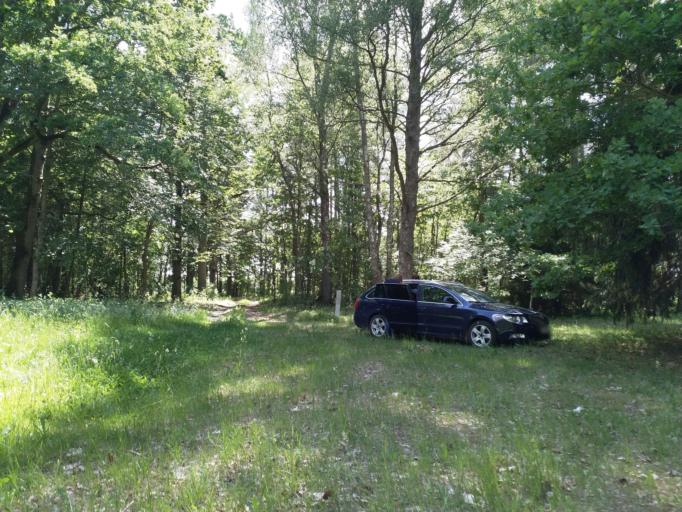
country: LV
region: Alsunga
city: Alsunga
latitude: 56.8805
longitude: 21.5733
